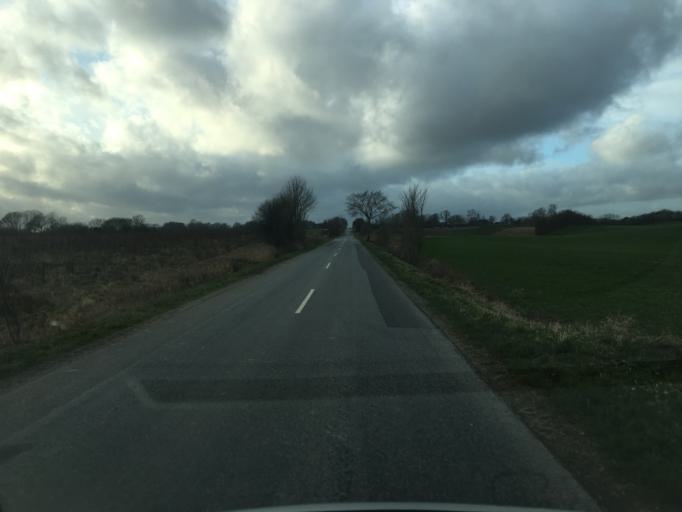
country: DK
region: South Denmark
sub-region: Sonderborg Kommune
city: Grasten
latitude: 54.9669
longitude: 9.5294
